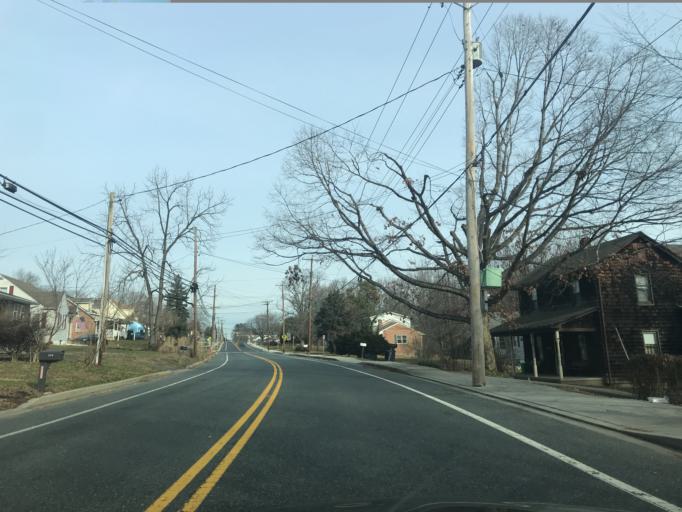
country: US
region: Maryland
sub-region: Harford County
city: Aberdeen
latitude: 39.5182
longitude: -76.1714
